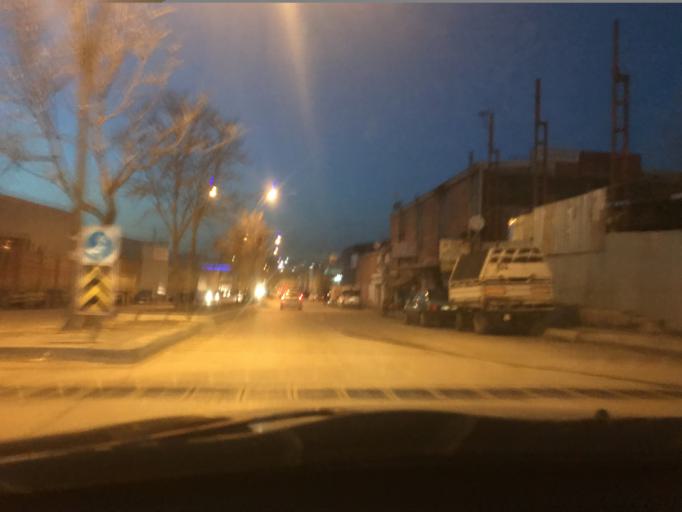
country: TR
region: Ankara
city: Batikent
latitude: 39.9702
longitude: 32.7412
